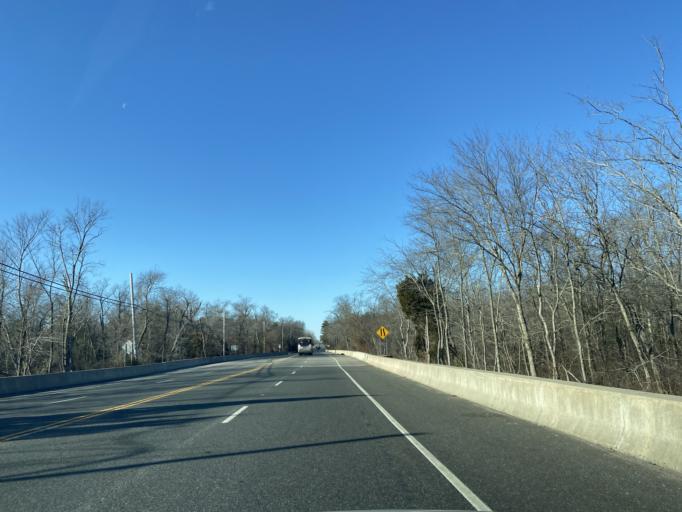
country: US
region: New Jersey
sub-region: Cumberland County
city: Vineland
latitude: 39.4885
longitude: -75.0743
